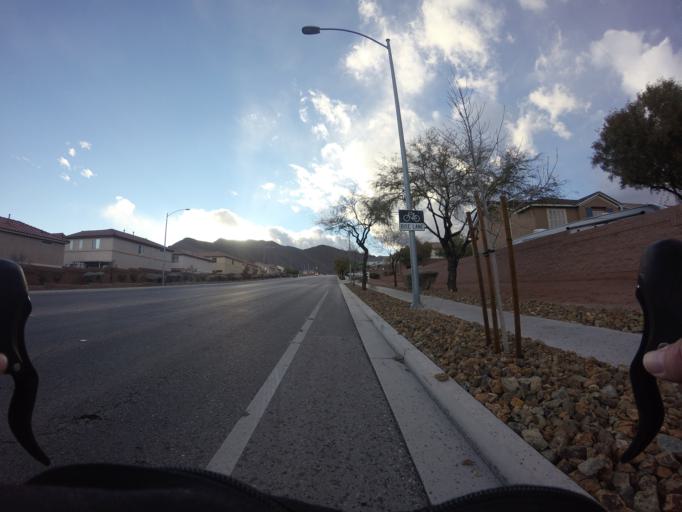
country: US
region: Nevada
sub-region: Clark County
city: Summerlin South
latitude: 36.2329
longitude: -115.3209
